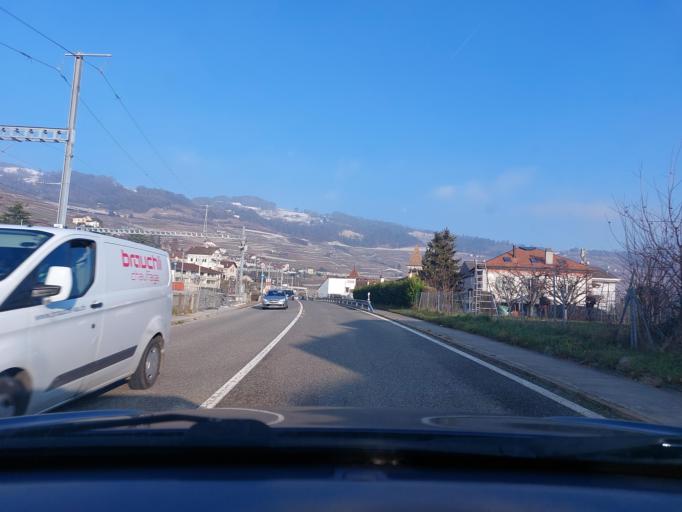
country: CH
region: Vaud
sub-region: Lavaux-Oron District
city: Cully
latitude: 46.4880
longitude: 6.7268
